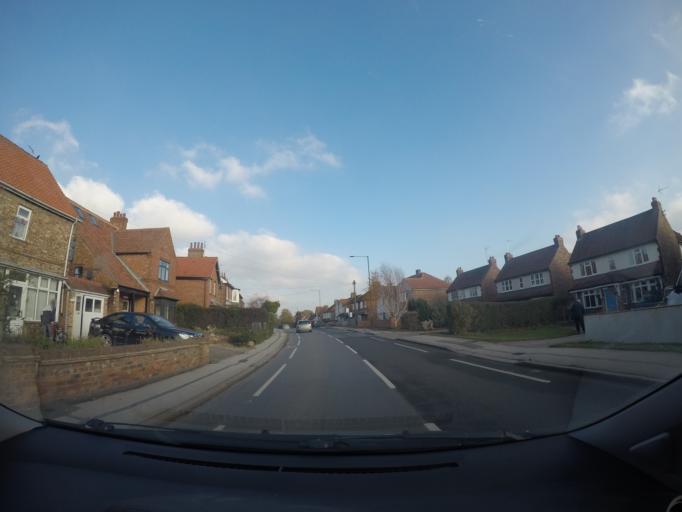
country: GB
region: England
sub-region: City of York
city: Huntington
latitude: 53.9925
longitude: -1.0639
